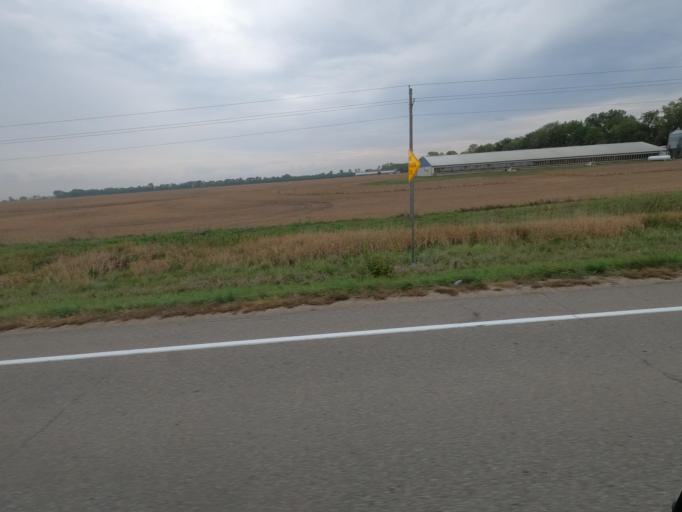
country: US
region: Iowa
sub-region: Van Buren County
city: Keosauqua
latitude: 40.8133
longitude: -91.7678
